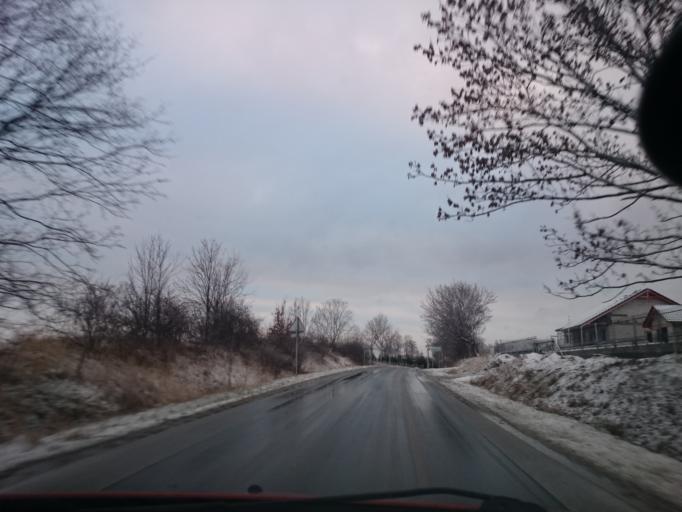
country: PL
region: Lower Silesian Voivodeship
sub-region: Powiat zabkowicki
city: Bardo
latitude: 50.5417
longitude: 16.7282
